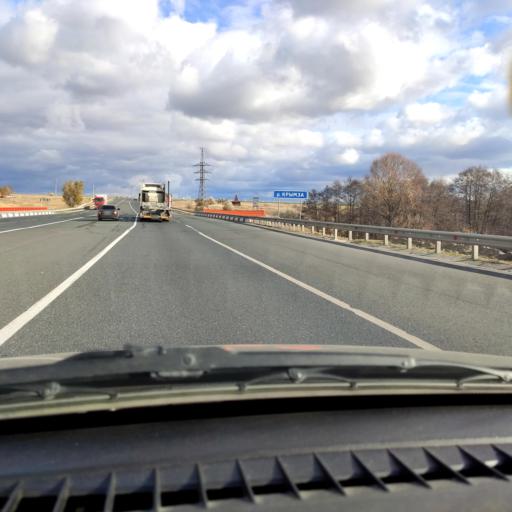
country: RU
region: Samara
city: Varlamovo
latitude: 53.2028
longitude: 48.3805
